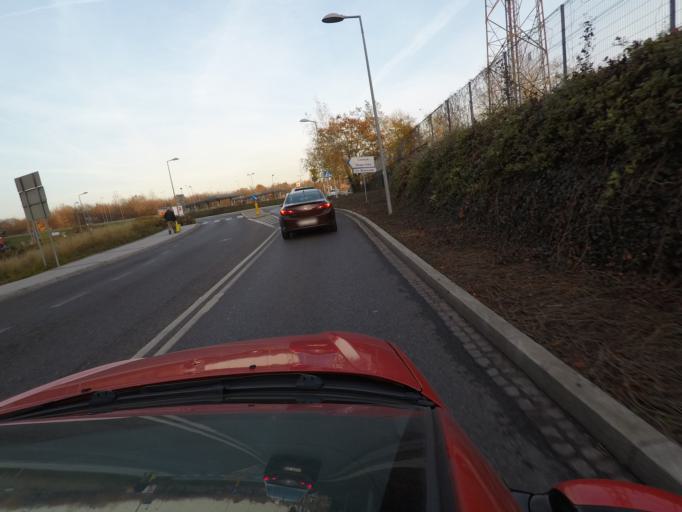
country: PL
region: Lesser Poland Voivodeship
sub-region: Krakow
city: Krakow
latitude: 50.0281
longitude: 19.9535
